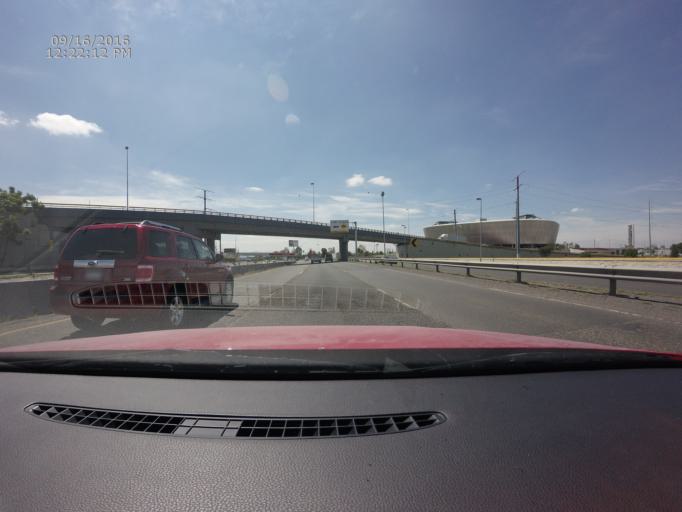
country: MX
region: Queretaro
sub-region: Queretaro
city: Sergio Villasenor
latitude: 20.6414
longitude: -100.4307
